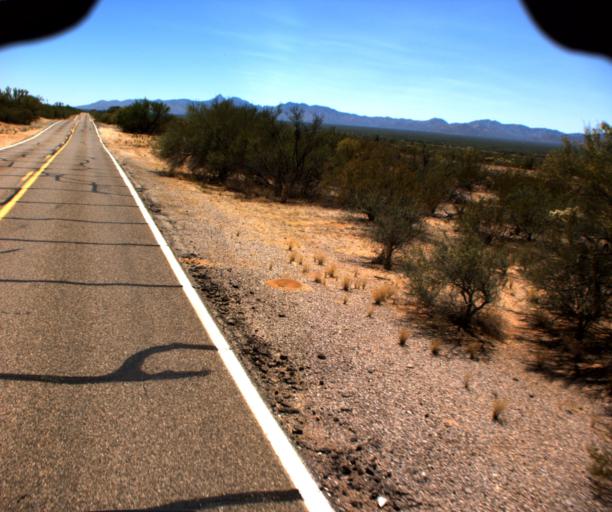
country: US
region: Arizona
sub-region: Pima County
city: Three Points
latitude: 31.9895
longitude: -111.3694
